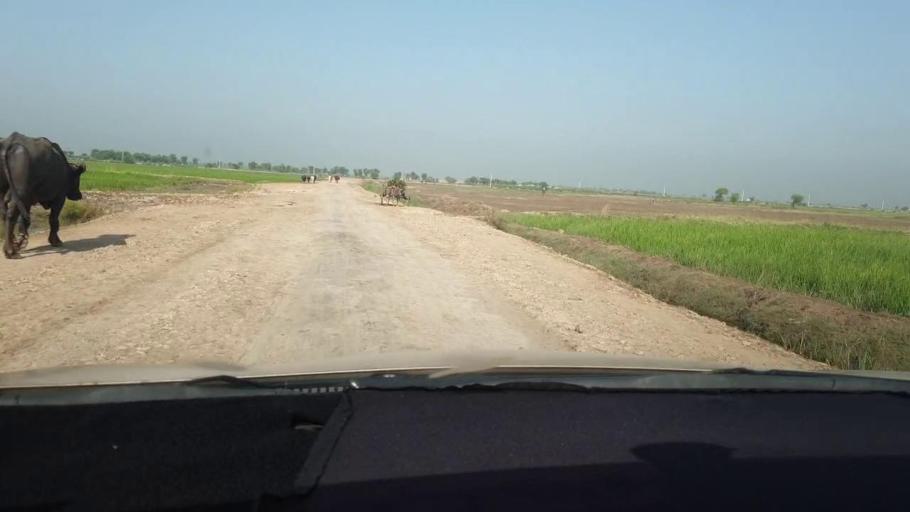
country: PK
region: Sindh
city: Miro Khan
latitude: 27.7568
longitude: 68.1381
